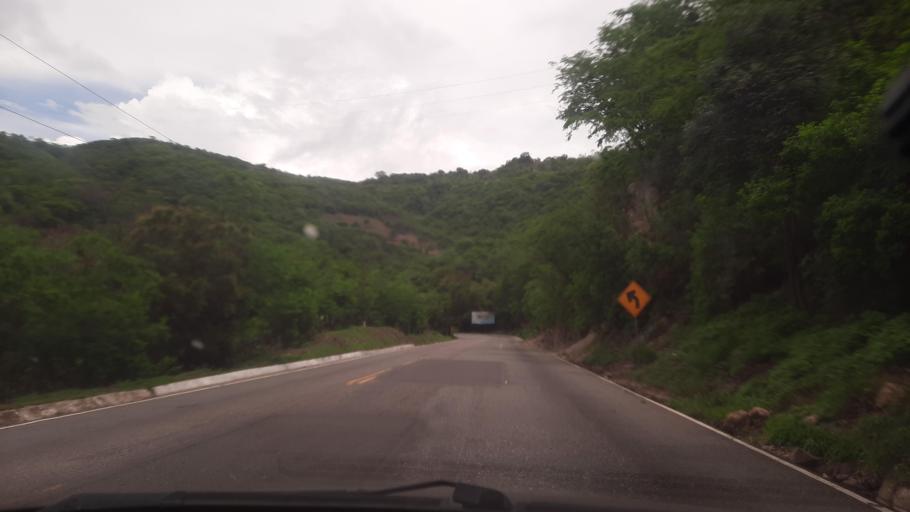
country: GT
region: Zacapa
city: San Jorge
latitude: 14.8844
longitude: -89.5184
